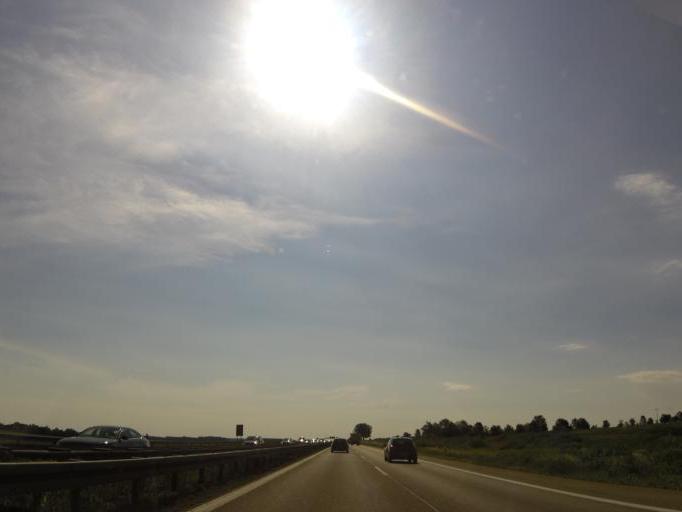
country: DE
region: Baden-Wuerttemberg
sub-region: Tuebingen Region
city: Merklingen
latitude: 48.5238
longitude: 9.7333
